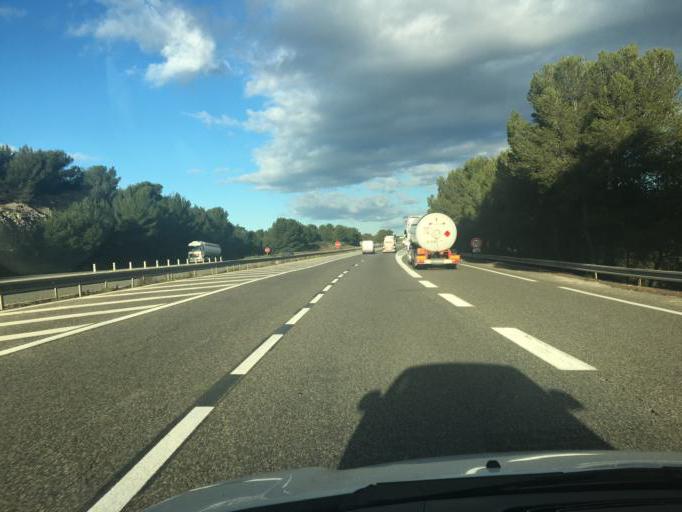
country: FR
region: Provence-Alpes-Cote d'Azur
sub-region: Departement des Bouches-du-Rhone
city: Martigues
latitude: 43.3950
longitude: 5.0509
